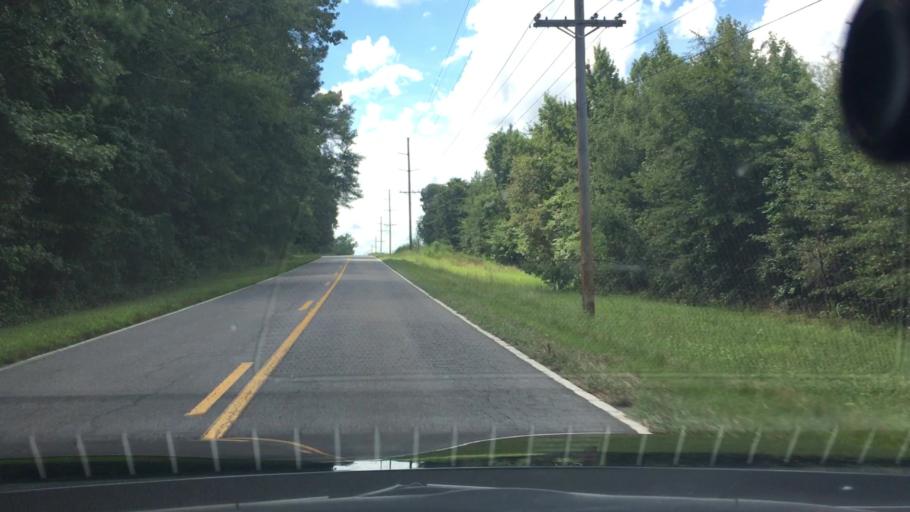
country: US
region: Georgia
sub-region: Putnam County
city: Jefferson
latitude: 33.3683
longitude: -83.2870
